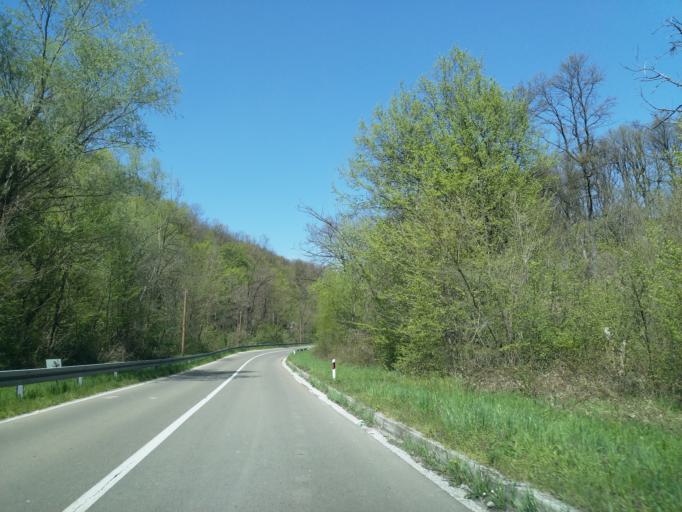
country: RS
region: Central Serbia
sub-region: Belgrade
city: Lazarevac
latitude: 44.3569
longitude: 20.3515
